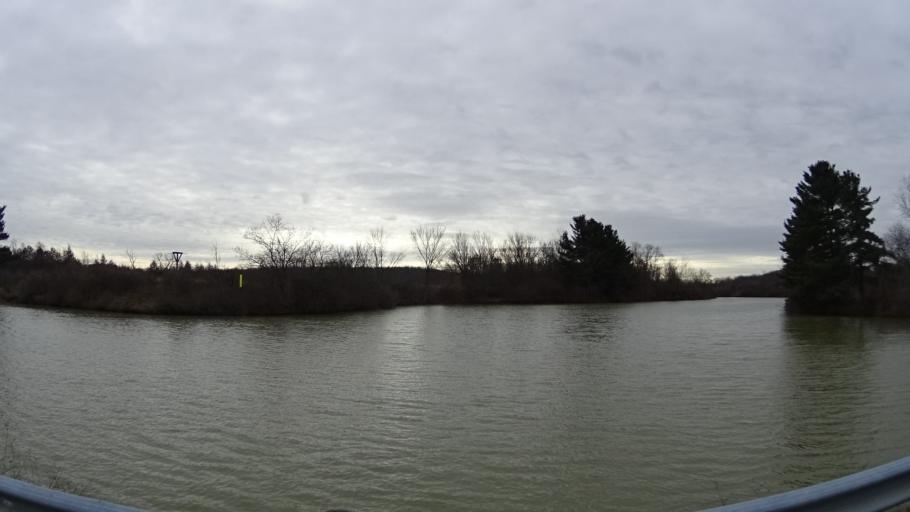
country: US
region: Ohio
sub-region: Lorain County
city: Wellington
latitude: 41.1484
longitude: -82.2395
